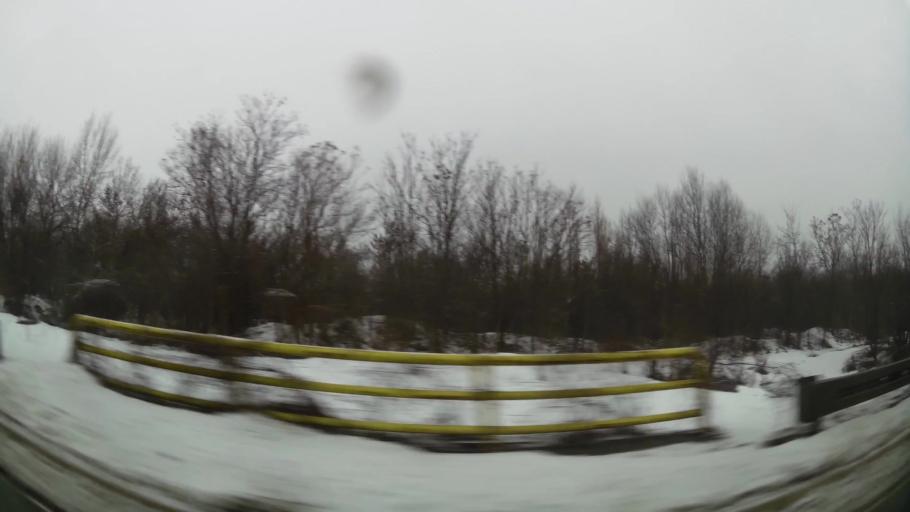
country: RS
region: Central Serbia
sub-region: Belgrade
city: Cukarica
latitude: 44.7604
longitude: 20.3871
